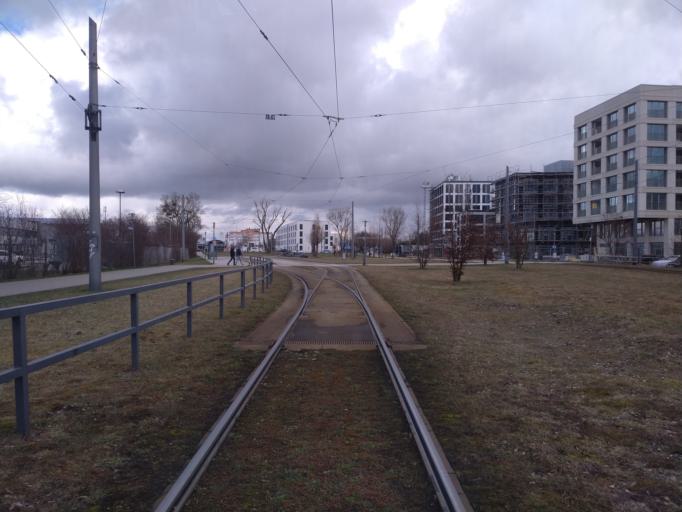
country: DE
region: Bavaria
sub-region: Upper Bavaria
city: Bogenhausen
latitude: 48.1859
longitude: 11.5908
